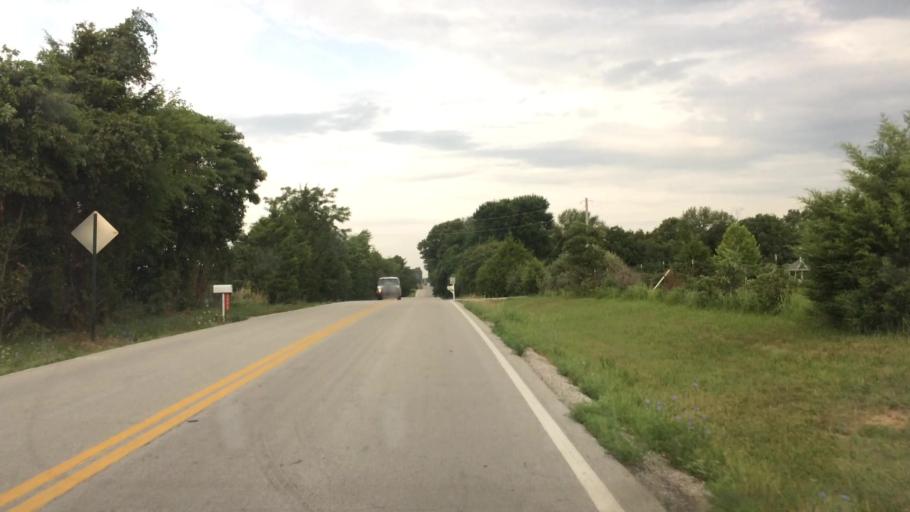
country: US
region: Missouri
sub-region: Greene County
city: Strafford
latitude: 37.2721
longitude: -93.1890
